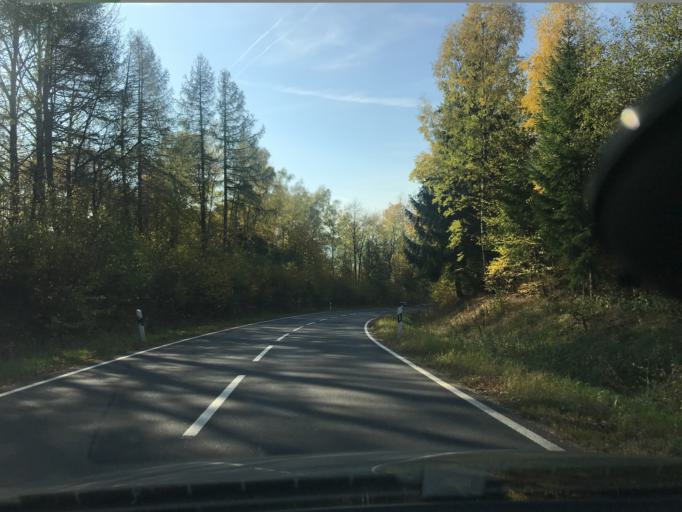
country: DE
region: Hesse
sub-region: Regierungsbezirk Kassel
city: Grossalmerode
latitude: 51.2095
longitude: 9.8305
